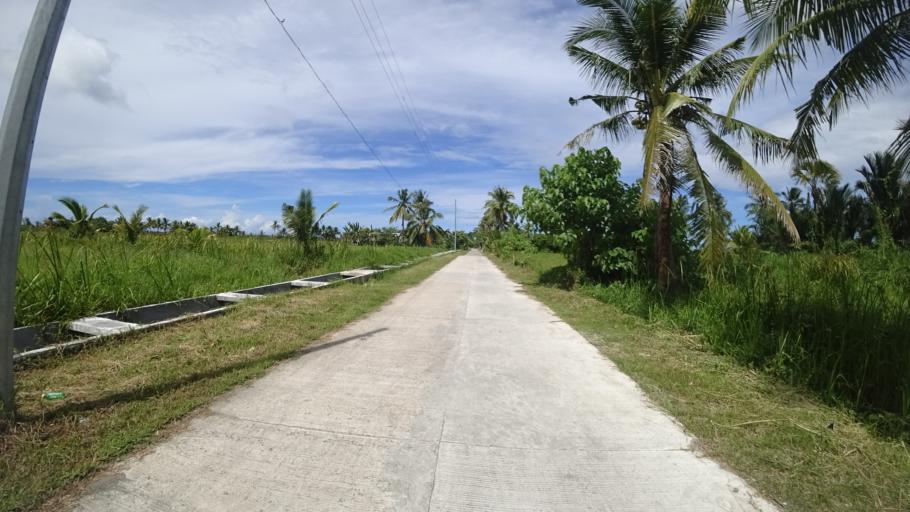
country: PH
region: Eastern Visayas
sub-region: Province of Leyte
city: MacArthur
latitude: 10.8587
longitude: 124.9724
